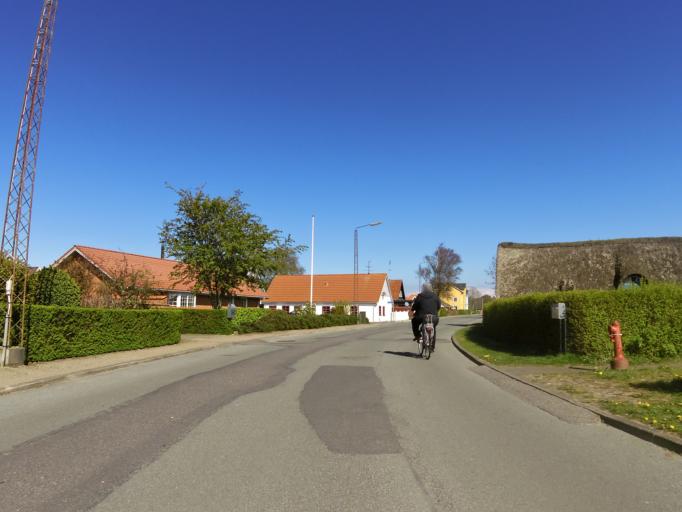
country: DK
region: South Denmark
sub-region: Tonder Kommune
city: Sherrebek
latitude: 55.1558
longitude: 8.7635
